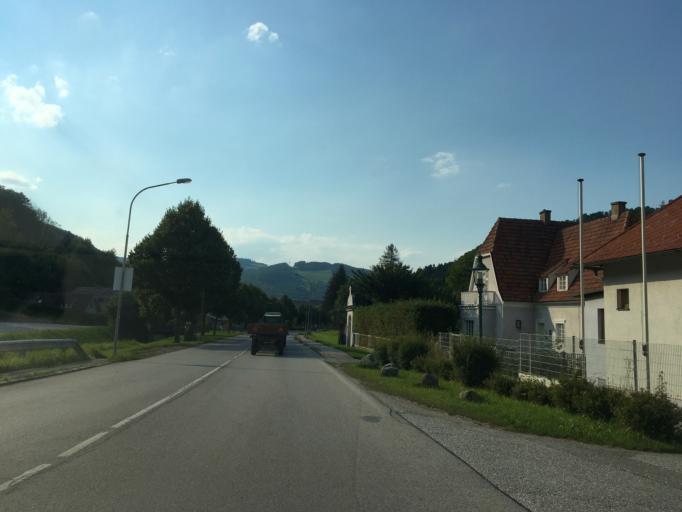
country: AT
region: Lower Austria
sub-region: Politischer Bezirk Neunkirchen
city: Edlitz
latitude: 47.5993
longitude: 16.1389
